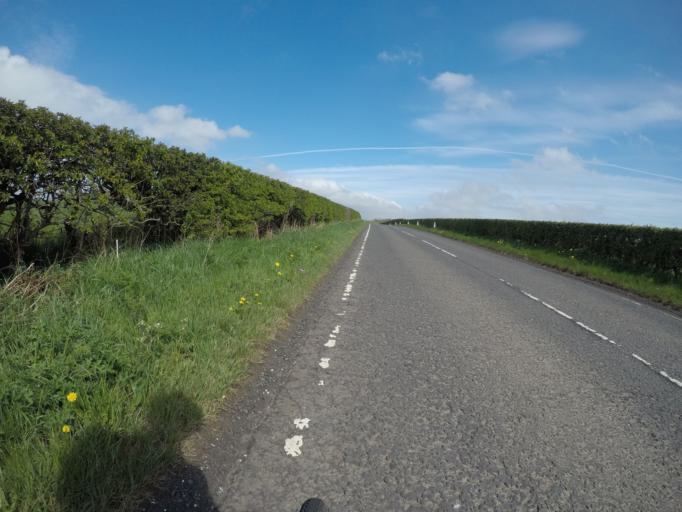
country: GB
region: Scotland
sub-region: East Ayrshire
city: Stewarton
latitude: 55.6685
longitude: -4.5331
